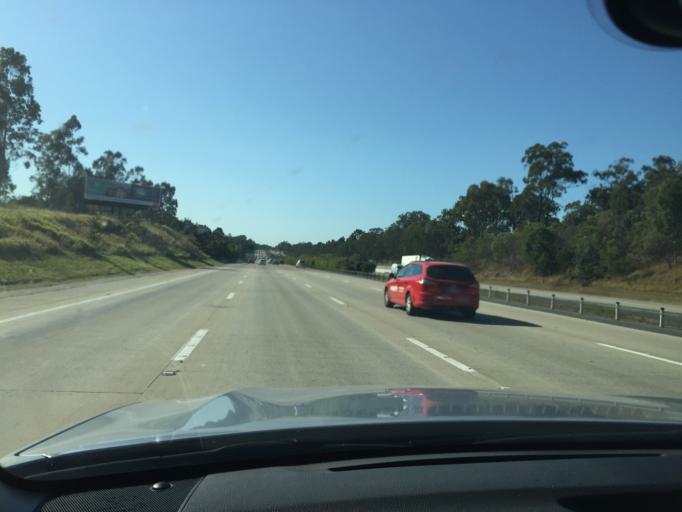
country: AU
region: Queensland
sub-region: Gold Coast
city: Ormeau Hills
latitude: -27.8138
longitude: 153.2755
